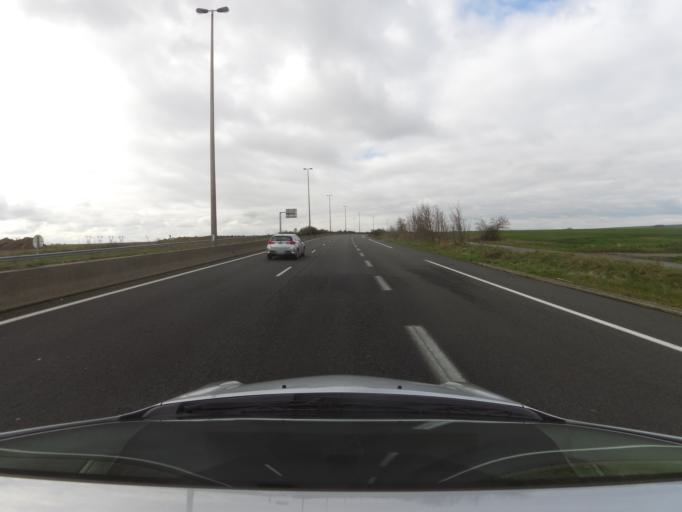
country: FR
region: Nord-Pas-de-Calais
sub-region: Departement du Pas-de-Calais
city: Coquelles
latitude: 50.9114
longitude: 1.7840
